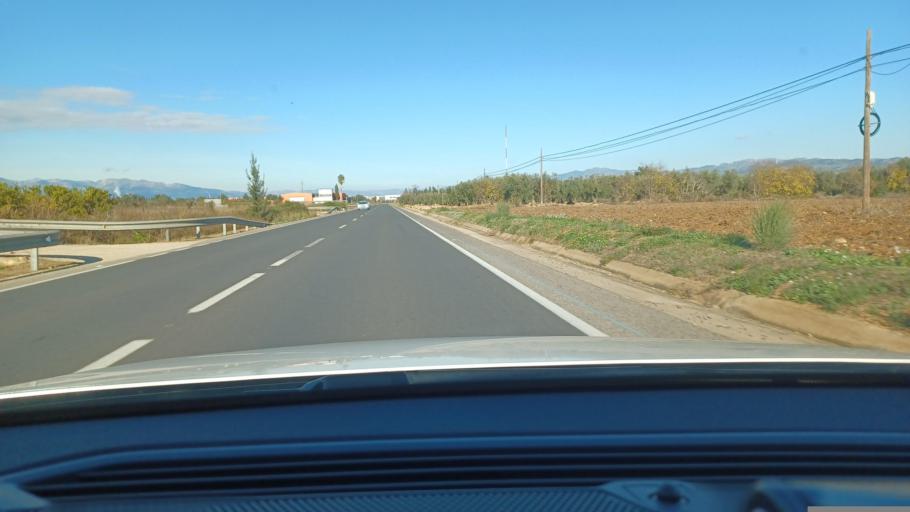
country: ES
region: Catalonia
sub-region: Provincia de Tarragona
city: Santa Barbara
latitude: 40.7286
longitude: 0.5033
